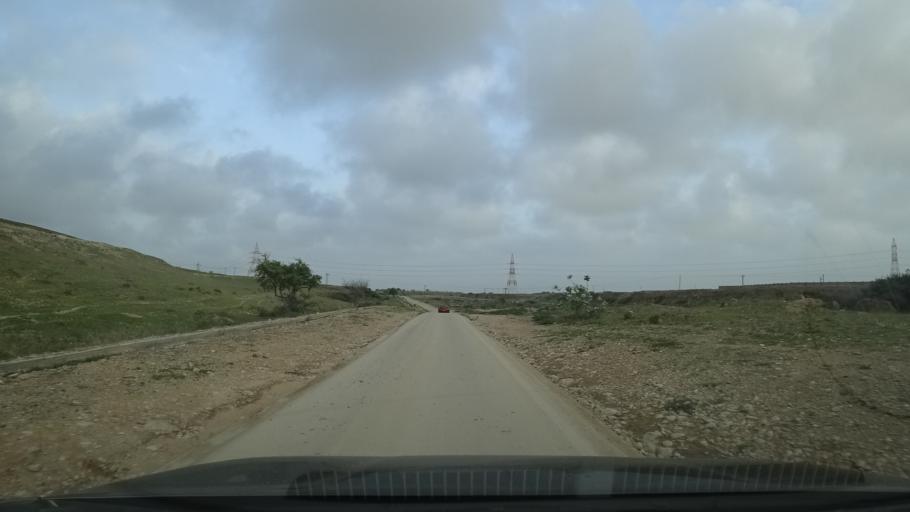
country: OM
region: Zufar
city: Salalah
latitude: 17.1082
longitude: 54.2291
